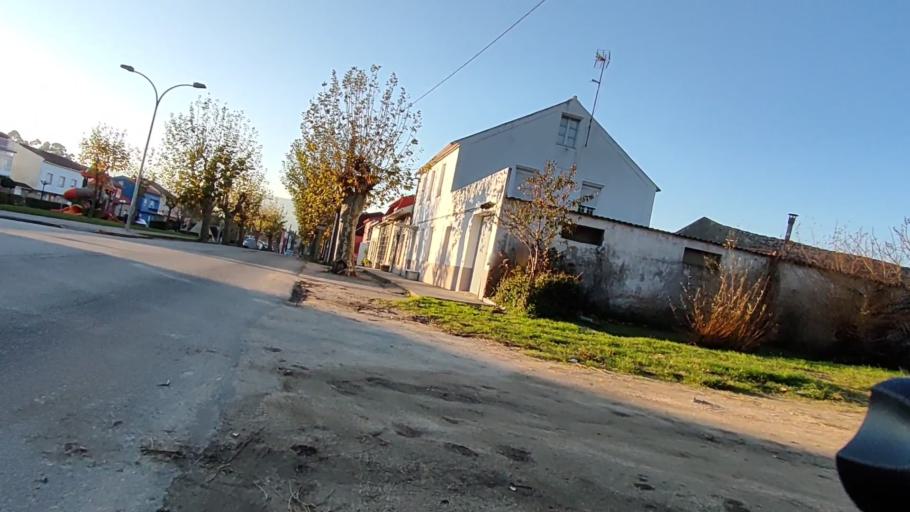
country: ES
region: Galicia
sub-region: Provincia da Coruna
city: Boiro
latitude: 42.6395
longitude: -8.8591
